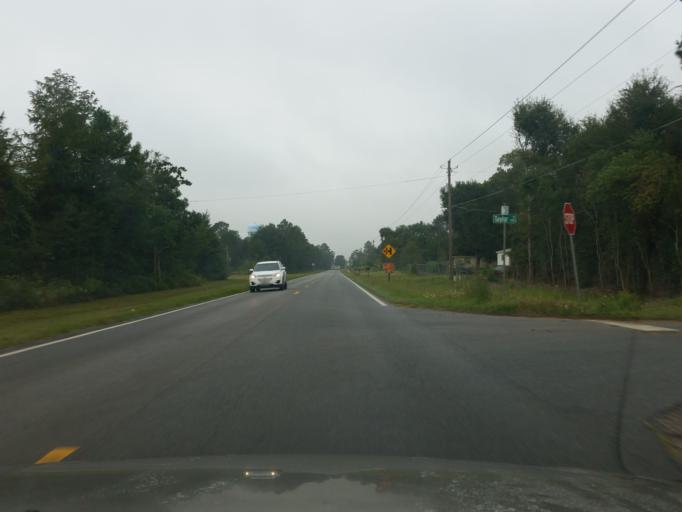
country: US
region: Florida
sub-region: Escambia County
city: Cantonment
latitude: 30.6065
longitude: -87.3385
